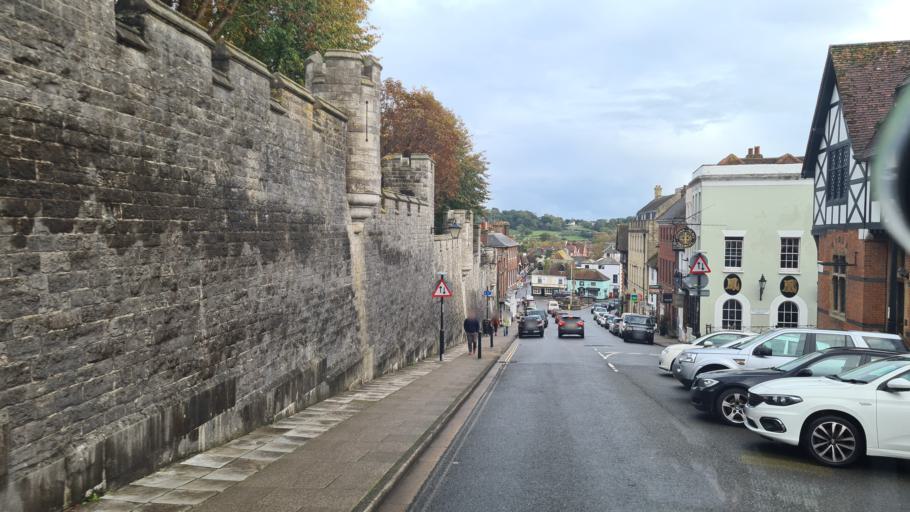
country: GB
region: England
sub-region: West Sussex
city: Arundel
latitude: 50.8554
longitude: -0.5552
